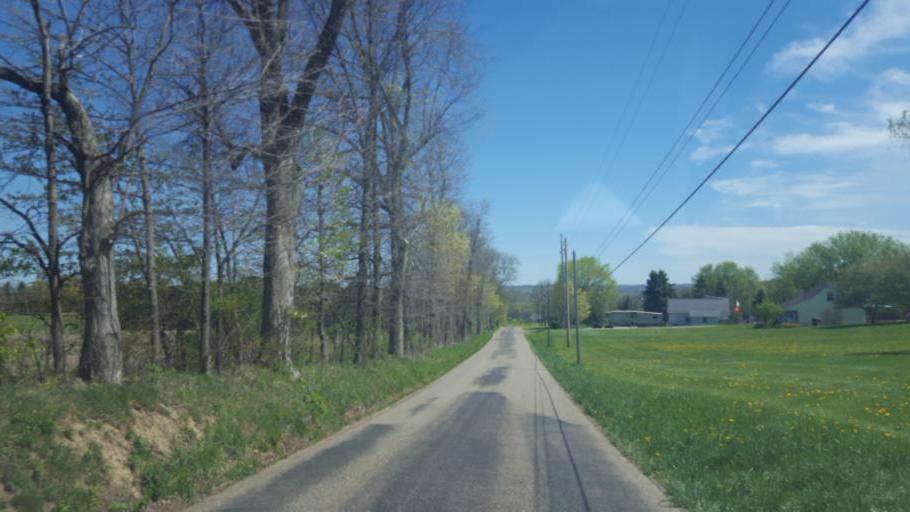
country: US
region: Ohio
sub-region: Richland County
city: Lincoln Heights
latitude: 40.6913
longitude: -82.4217
